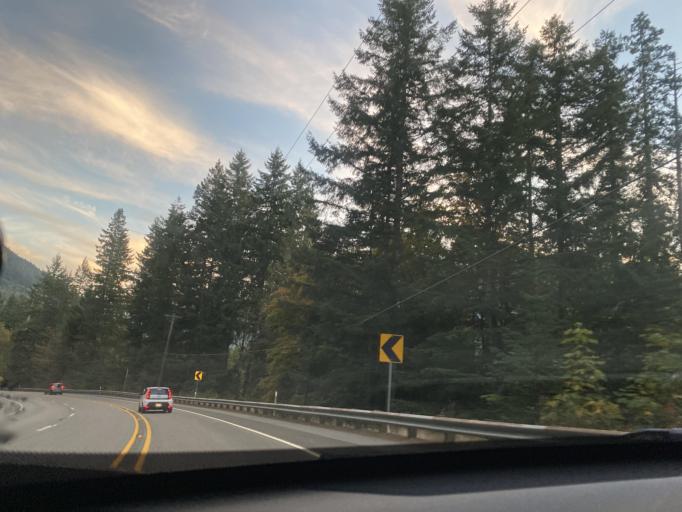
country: US
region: Washington
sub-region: Clallam County
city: Port Angeles
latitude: 48.0697
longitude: -123.5756
